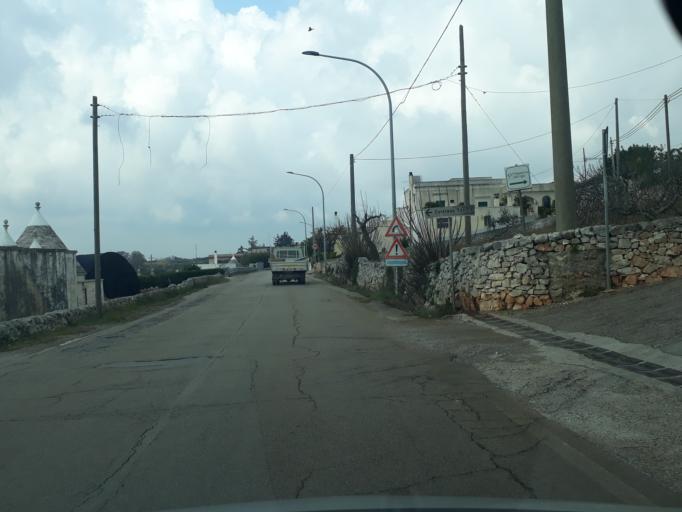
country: IT
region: Apulia
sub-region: Provincia di Brindisi
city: Cisternino
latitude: 40.7450
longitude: 17.3992
